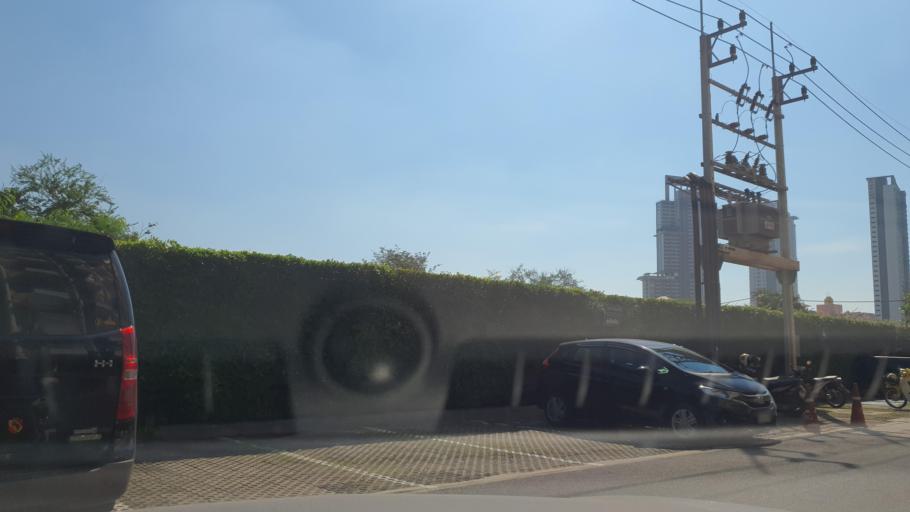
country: TH
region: Chon Buri
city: Phatthaya
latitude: 12.8631
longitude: 100.9027
